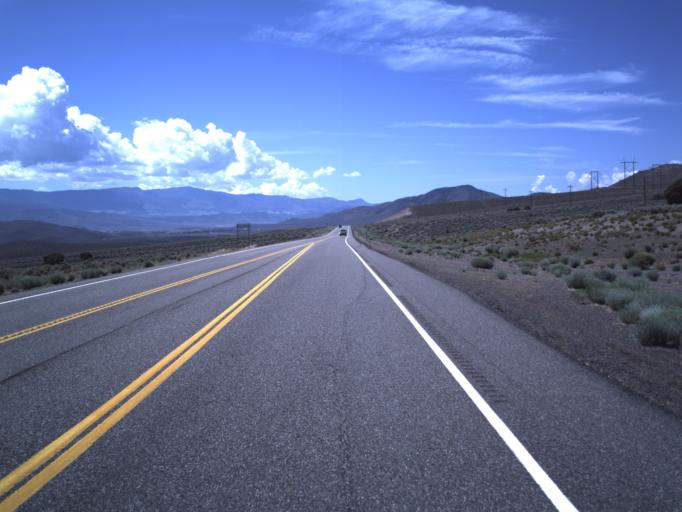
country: US
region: Utah
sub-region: Piute County
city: Junction
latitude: 38.3258
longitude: -112.2190
